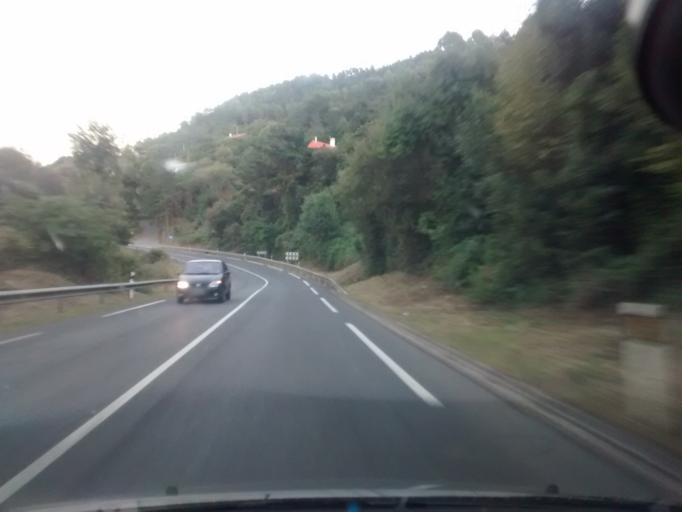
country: ES
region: Basque Country
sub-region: Provincia de Guipuzcoa
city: Mutriku
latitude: 43.3051
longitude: -2.3676
